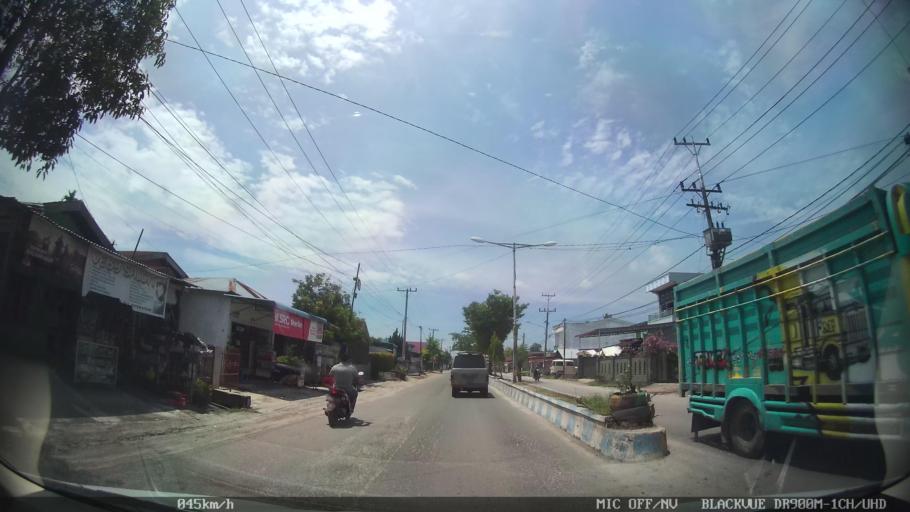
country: ID
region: North Sumatra
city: Percut
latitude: 3.5489
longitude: 98.8795
